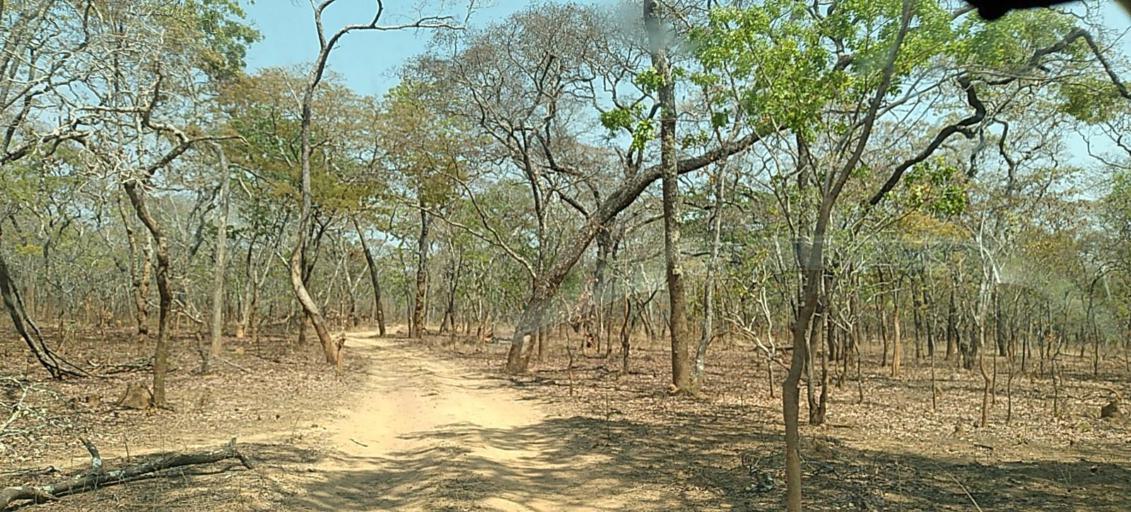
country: ZM
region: North-Western
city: Kasempa
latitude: -13.3928
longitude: 25.6127
